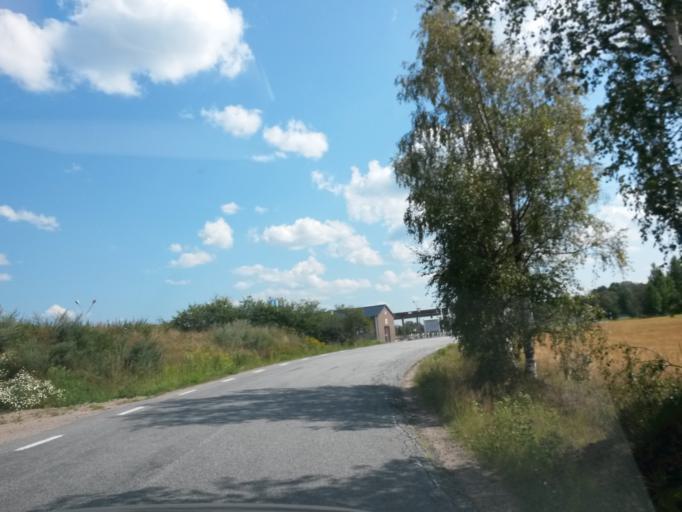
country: SE
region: Vaestra Goetaland
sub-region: Herrljunga Kommun
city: Herrljunga
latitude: 58.0894
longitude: 13.0126
